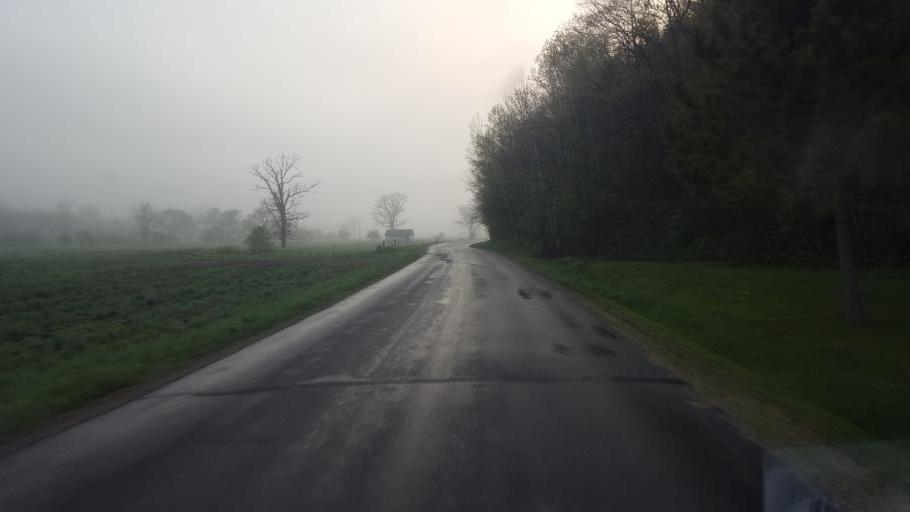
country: US
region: Wisconsin
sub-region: Vernon County
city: Hillsboro
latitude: 43.6235
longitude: -90.3672
